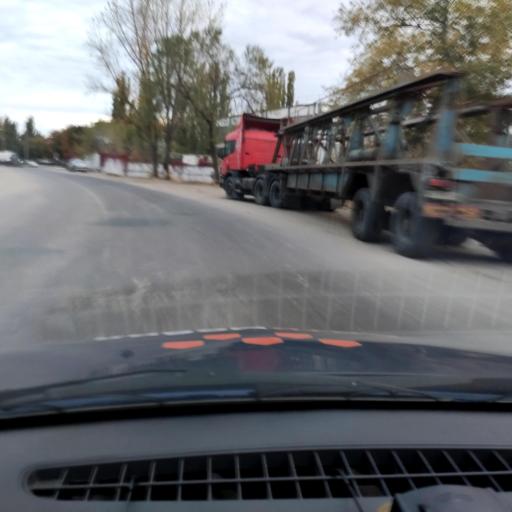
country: RU
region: Voronezj
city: Pridonskoy
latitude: 51.6771
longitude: 39.0917
